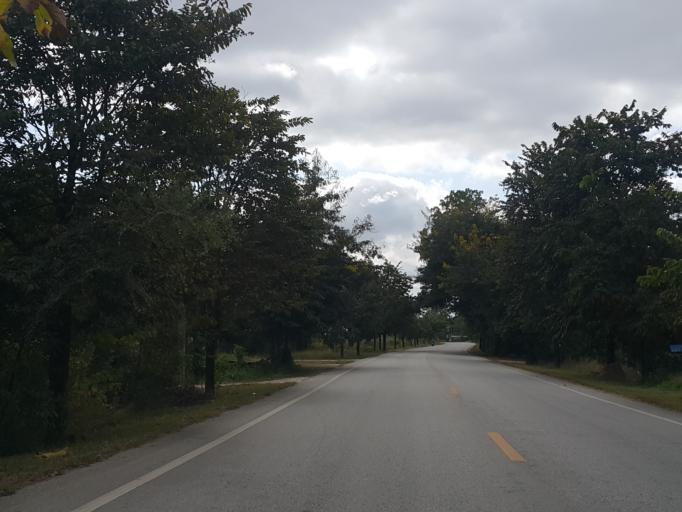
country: TH
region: Lamphun
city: Ban Thi
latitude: 18.6416
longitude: 99.1069
